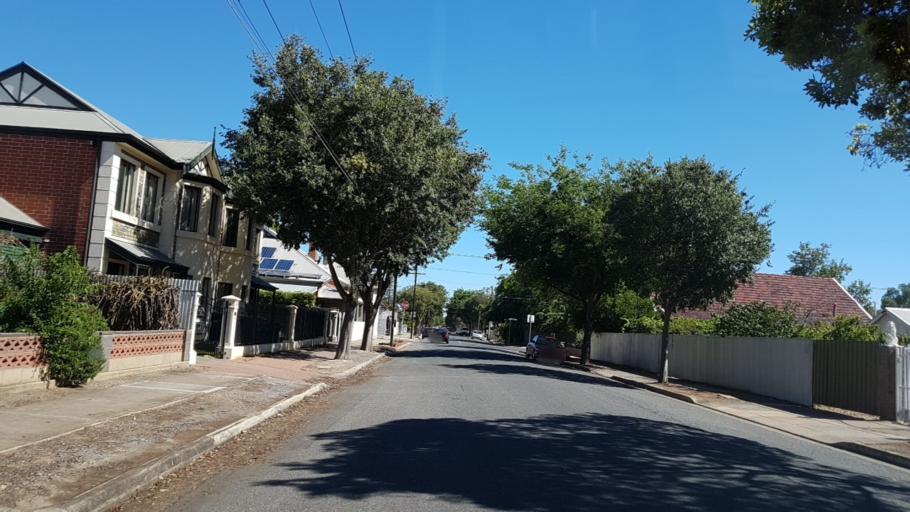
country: AU
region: South Australia
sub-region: City of West Torrens
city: Thebarton
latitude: -34.9177
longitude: 138.5608
